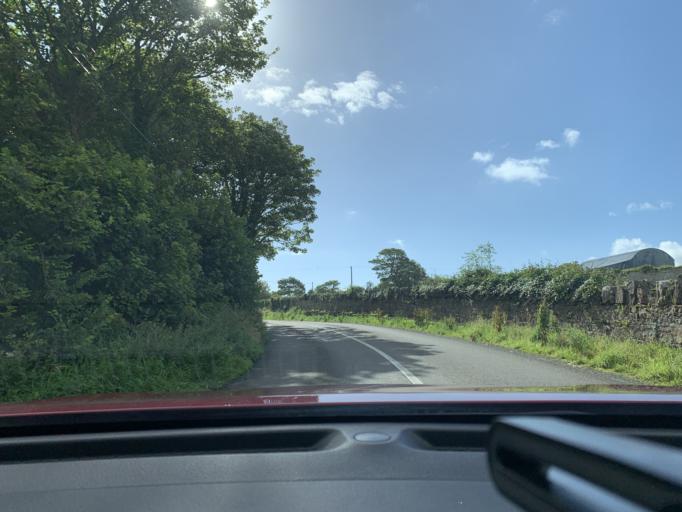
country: IE
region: Connaught
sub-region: Sligo
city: Strandhill
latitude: 54.3582
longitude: -8.5870
